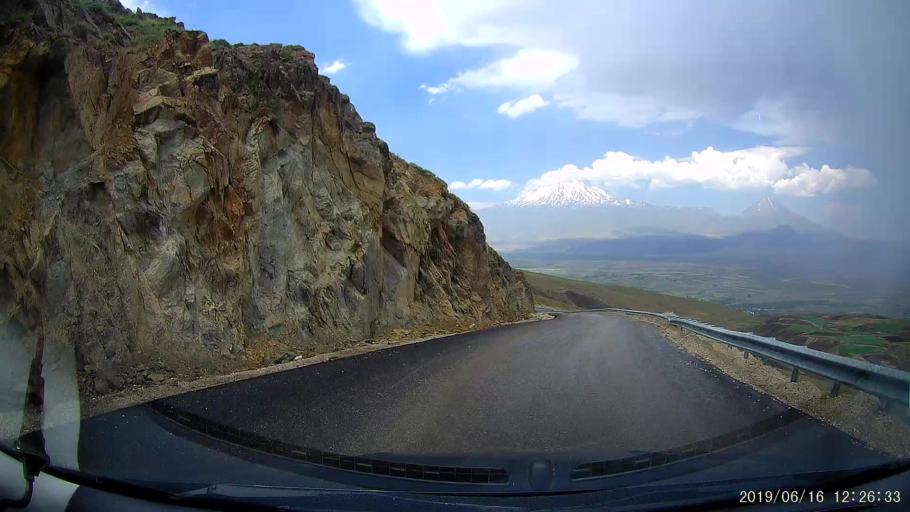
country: TR
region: Agri
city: Dogubayazit
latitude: 39.4454
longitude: 44.2360
